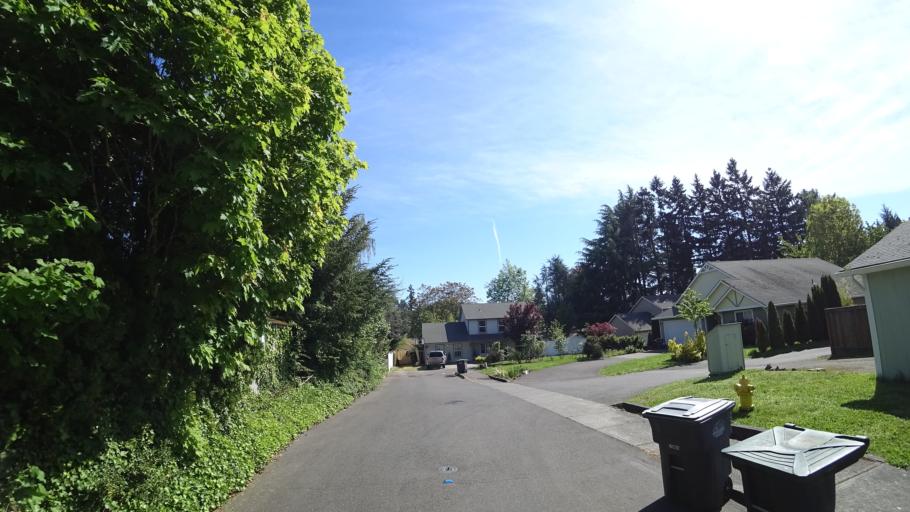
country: US
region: Oregon
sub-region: Washington County
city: Hillsboro
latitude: 45.5143
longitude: -122.9618
